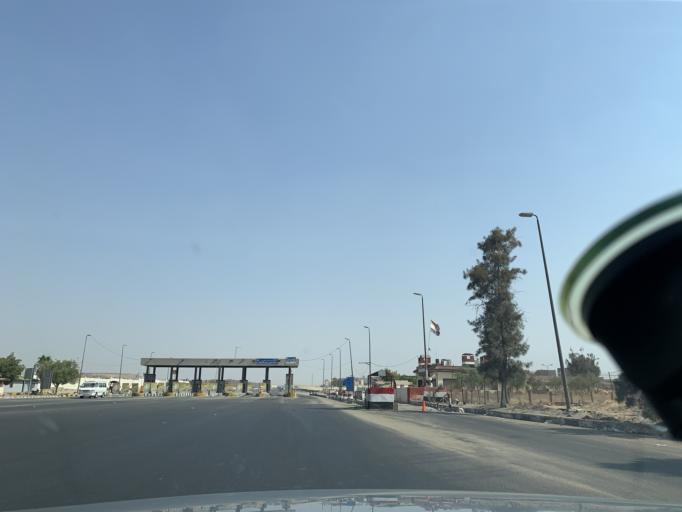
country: EG
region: Muhafazat al Qalyubiyah
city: Al Khankah
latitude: 30.1985
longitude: 31.4210
